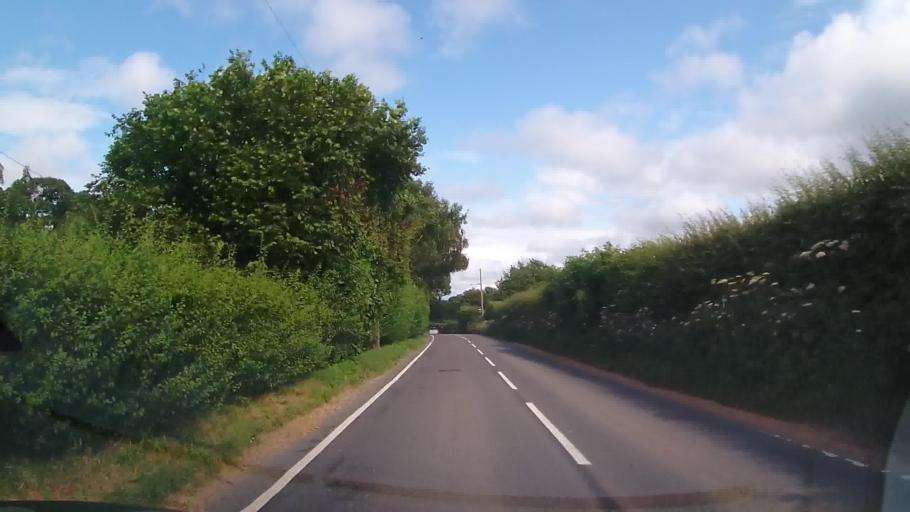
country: GB
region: England
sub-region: Shropshire
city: Great Ness
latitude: 52.7954
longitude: -2.9107
